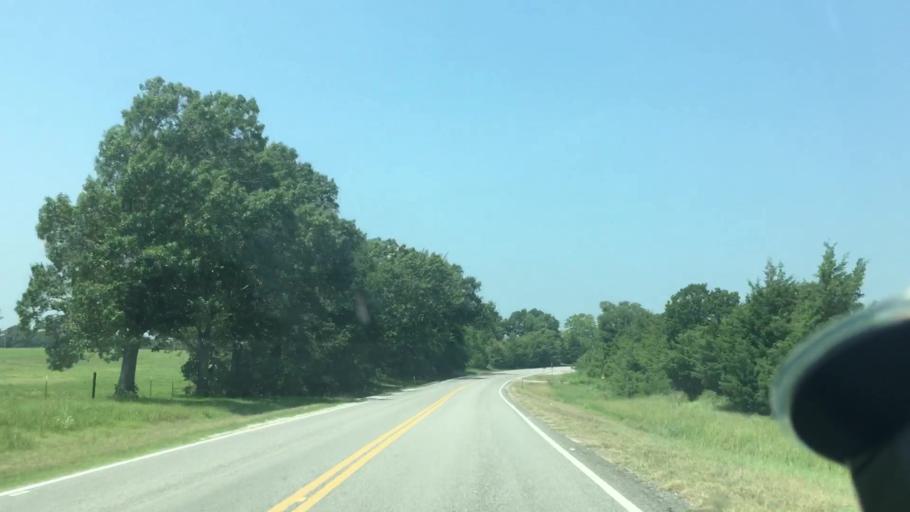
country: US
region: Oklahoma
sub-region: Atoka County
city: Atoka
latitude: 34.2802
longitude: -95.9478
